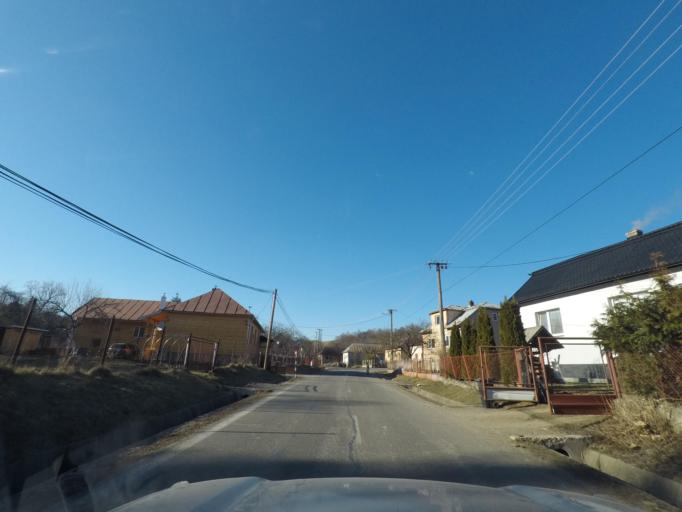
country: SK
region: Presovsky
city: Medzilaborce
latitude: 49.1939
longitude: 22.0026
